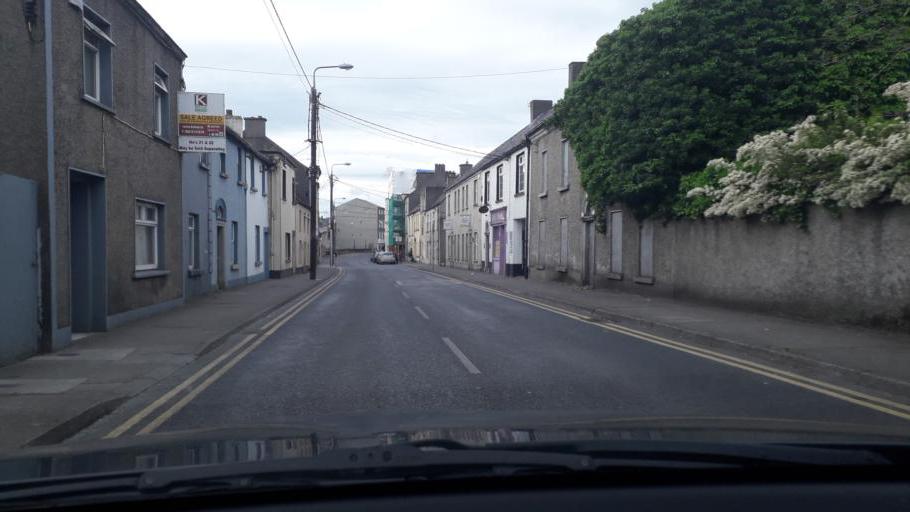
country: IE
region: Leinster
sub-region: County Carlow
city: Carlow
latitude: 52.8340
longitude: -6.9328
